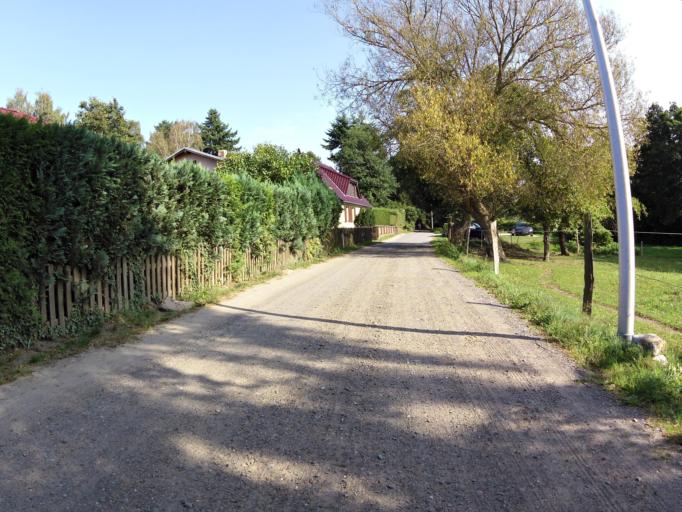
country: DE
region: Mecklenburg-Vorpommern
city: Seebad Bansin
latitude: 53.9594
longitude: 14.1389
